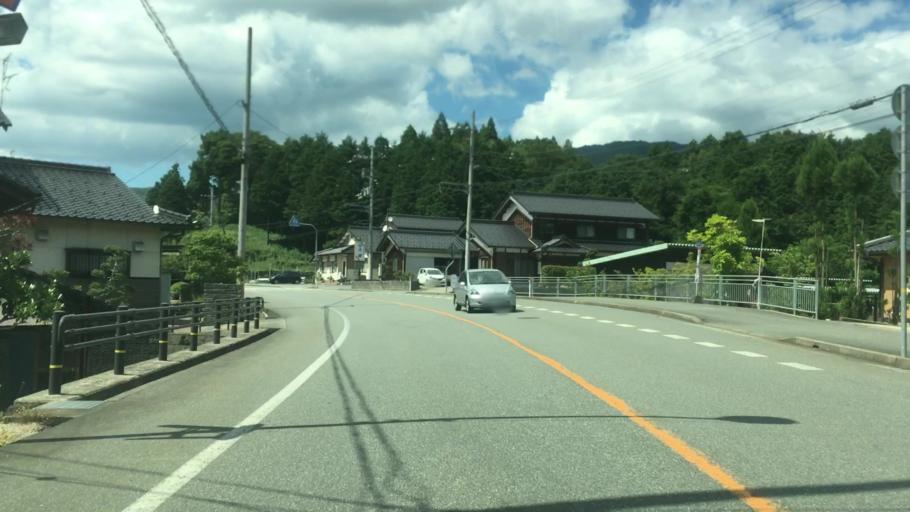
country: JP
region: Hyogo
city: Toyooka
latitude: 35.4805
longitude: 134.7085
